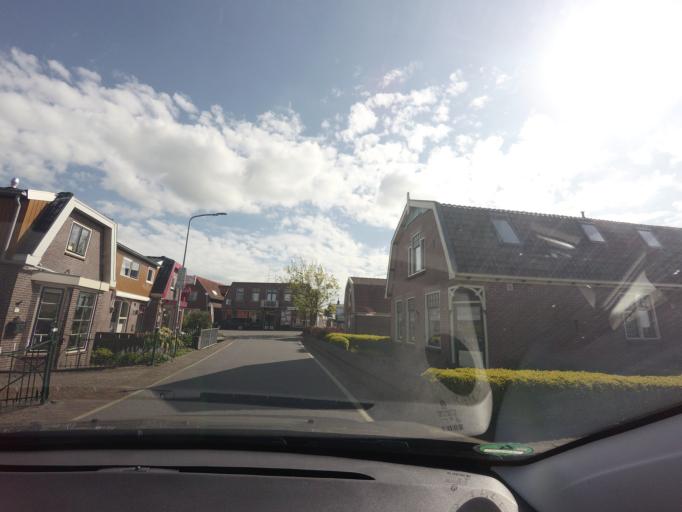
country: NL
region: North Holland
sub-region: Gemeente Heerhugowaard
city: Heerhugowaard
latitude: 52.6248
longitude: 4.8898
